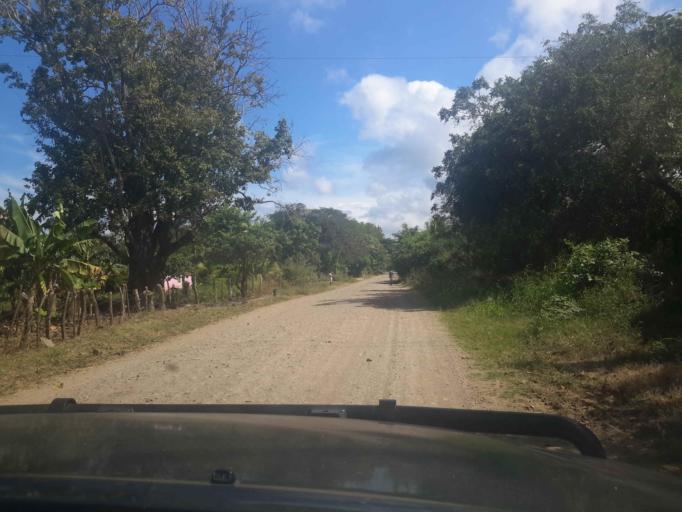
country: NI
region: Granada
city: Nandaime
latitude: 11.6622
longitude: -85.9568
